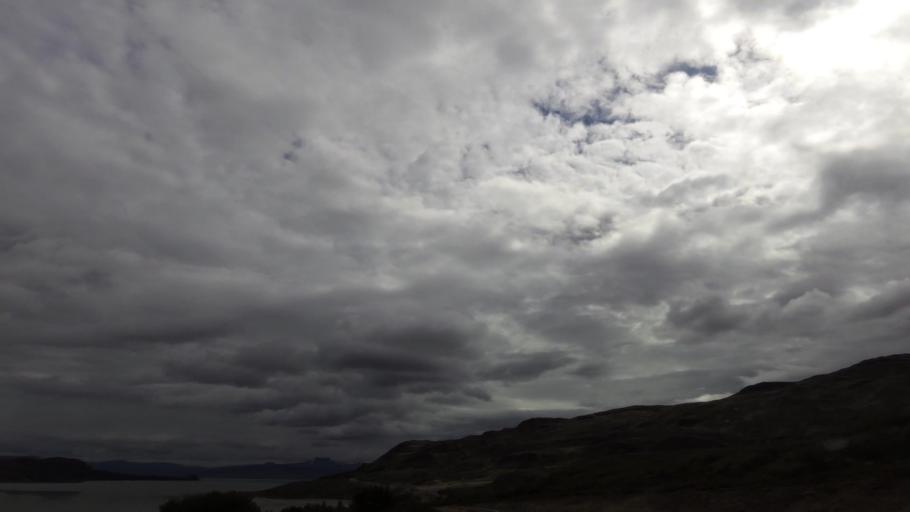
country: IS
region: West
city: Stykkisholmur
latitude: 65.5344
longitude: -22.1228
